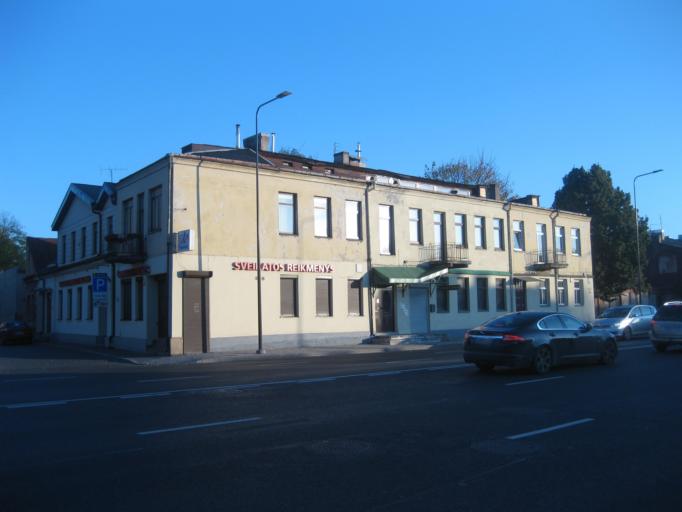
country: LT
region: Kauno apskritis
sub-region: Kaunas
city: Kaunas
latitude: 54.8961
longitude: 23.8958
